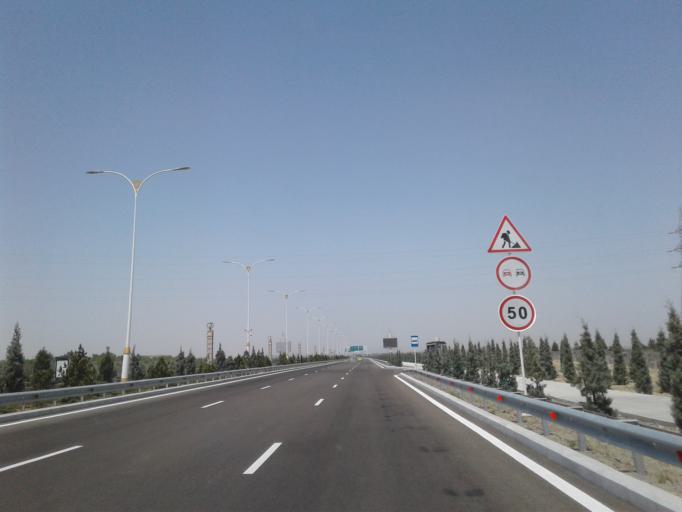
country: TM
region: Balkan
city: Turkmenbasy
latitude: 39.9671
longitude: 52.8657
